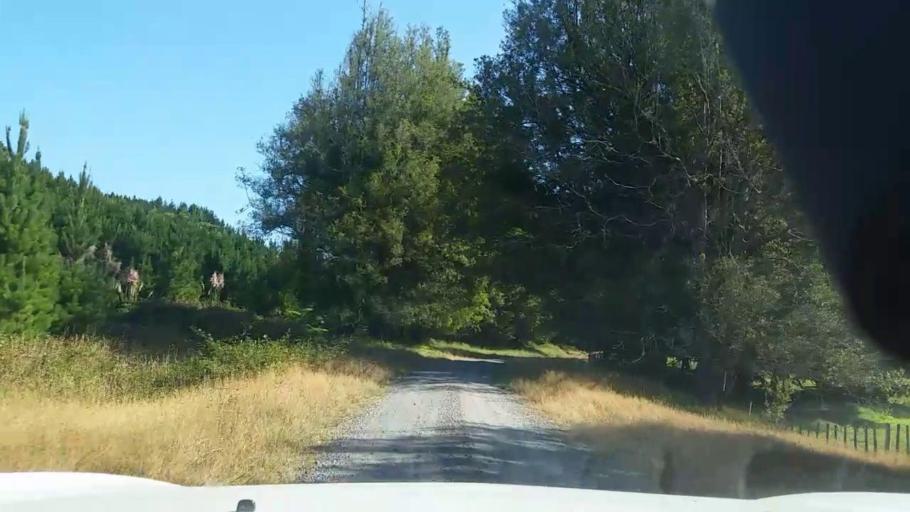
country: NZ
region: Bay of Plenty
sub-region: Western Bay of Plenty District
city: Maketu
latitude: -37.9710
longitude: 176.4087
